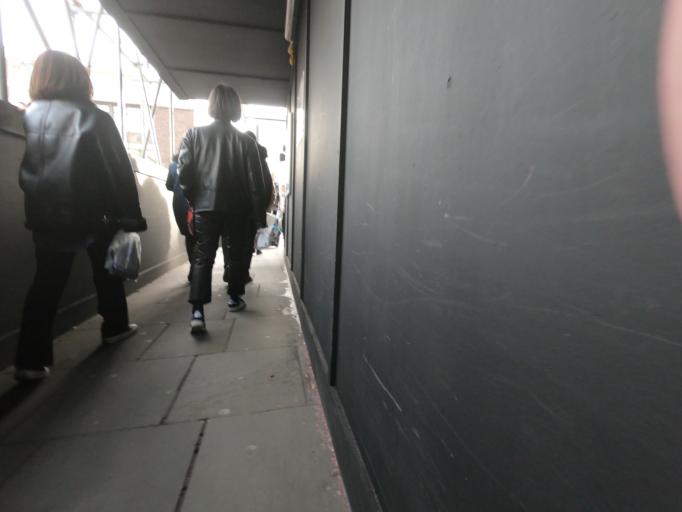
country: GB
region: England
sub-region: Greater London
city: Kensington
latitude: 51.5083
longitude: -0.1970
